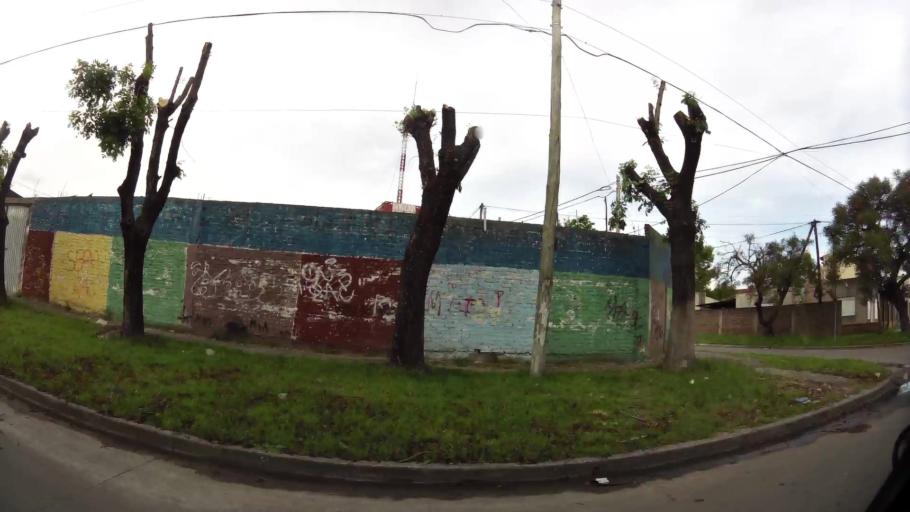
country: AR
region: Buenos Aires
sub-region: Partido de Quilmes
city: Quilmes
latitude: -34.7510
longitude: -58.2830
